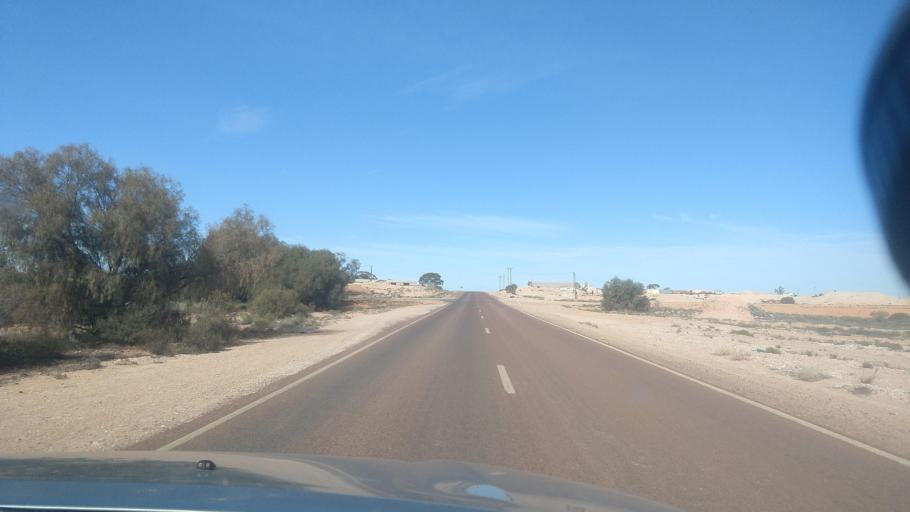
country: AU
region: South Australia
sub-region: Coober Pedy
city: Coober Pedy
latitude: -29.0170
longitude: 134.7452
